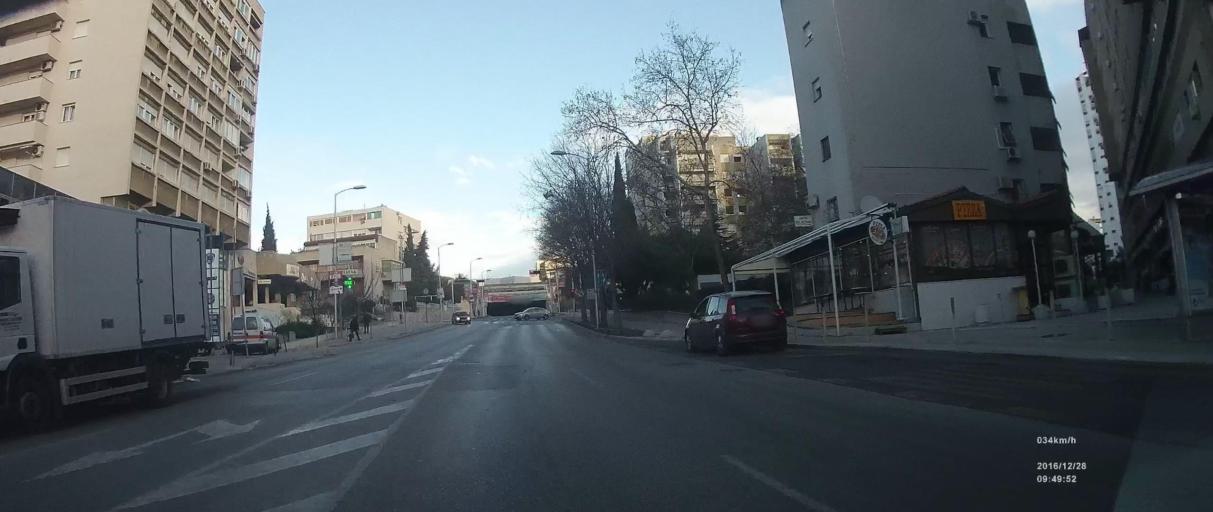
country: HR
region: Splitsko-Dalmatinska
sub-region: Grad Split
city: Split
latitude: 43.5057
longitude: 16.4562
